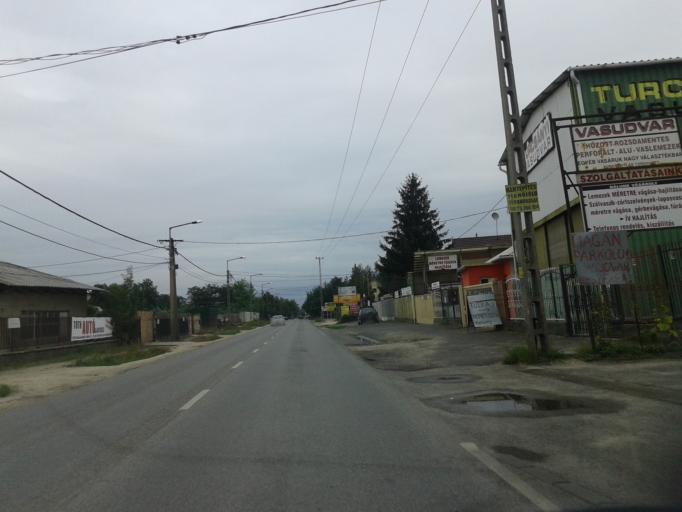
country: HU
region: Pest
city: Szigethalom
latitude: 47.3216
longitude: 19.0151
